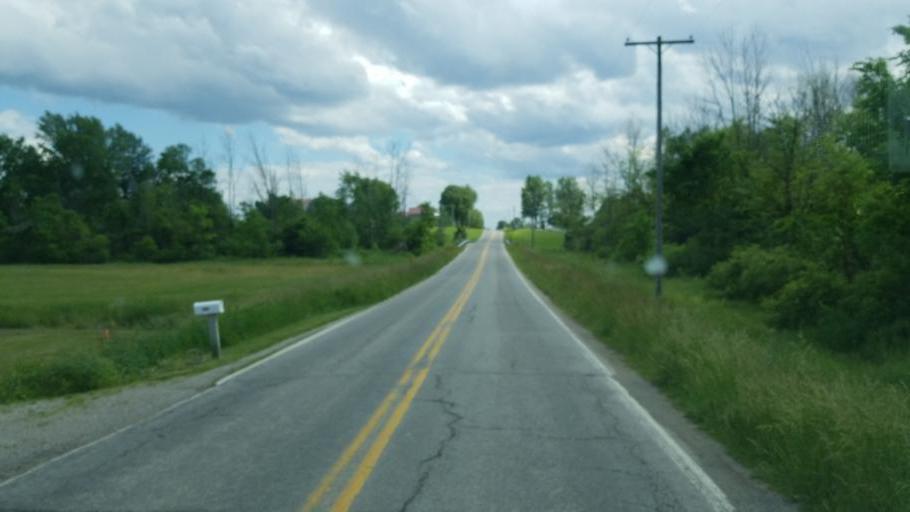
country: US
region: Ohio
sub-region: Huron County
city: Plymouth
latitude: 41.0106
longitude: -82.6069
